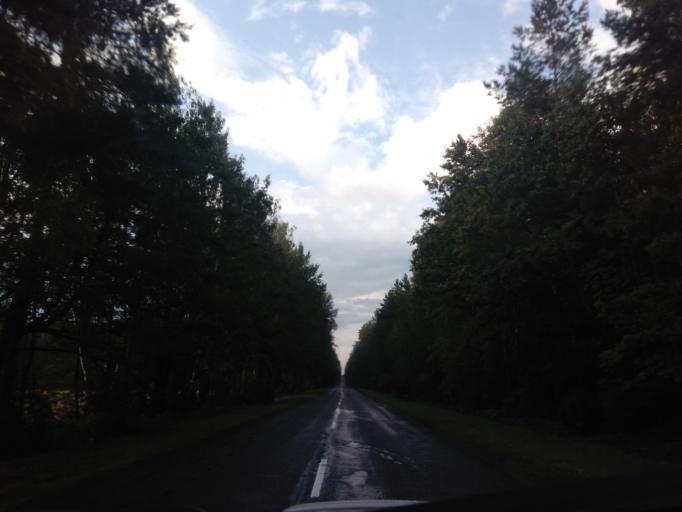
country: BY
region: Minsk
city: Uzda
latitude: 53.3579
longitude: 27.0994
